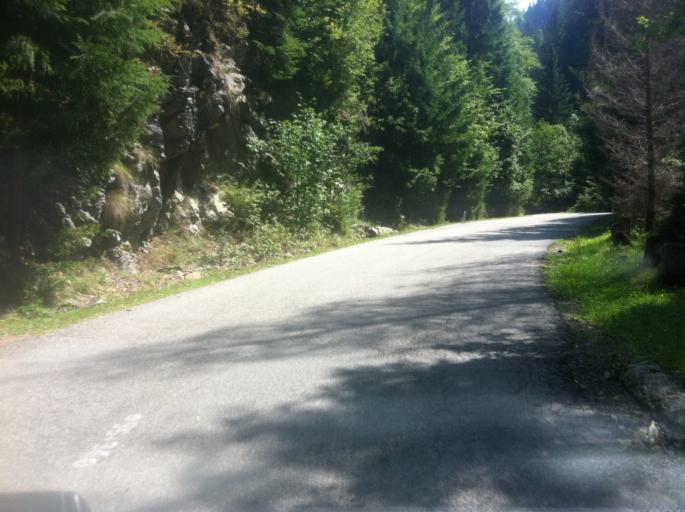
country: RO
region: Hunedoara
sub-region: Oras Petrila
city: Petrila
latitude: 45.4082
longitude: 23.5145
